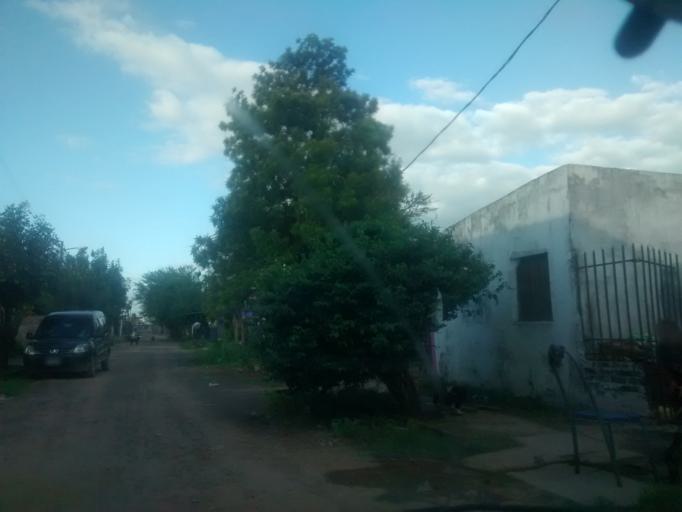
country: AR
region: Chaco
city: Fontana
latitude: -27.4488
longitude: -59.0246
